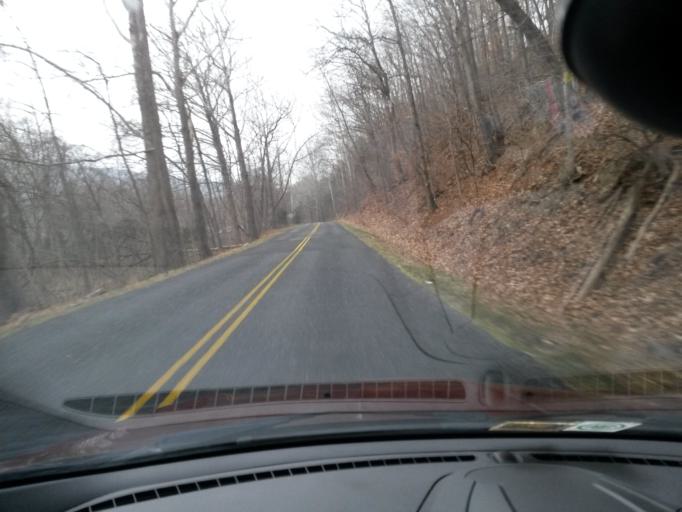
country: US
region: Virginia
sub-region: City of Lexington
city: Lexington
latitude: 37.8693
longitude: -79.5526
